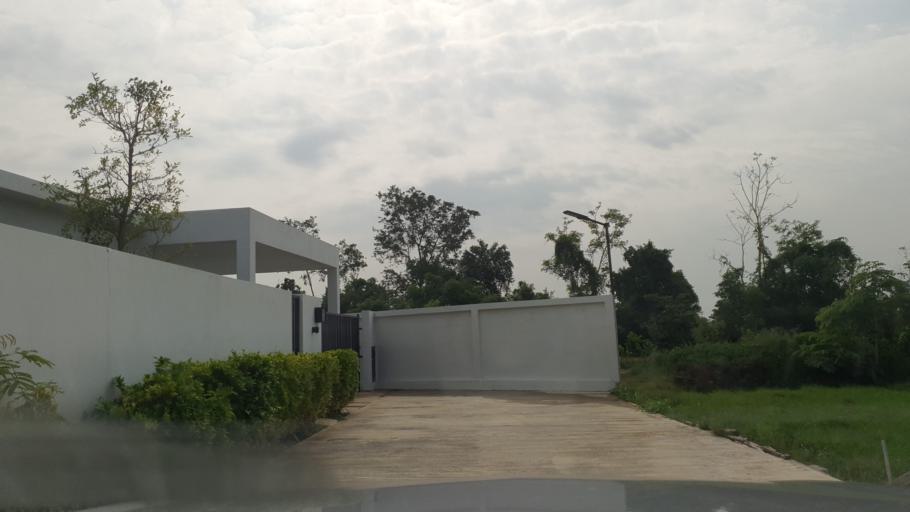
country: TH
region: Phitsanulok
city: Bang Rakam
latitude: 16.8031
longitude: 100.1631
